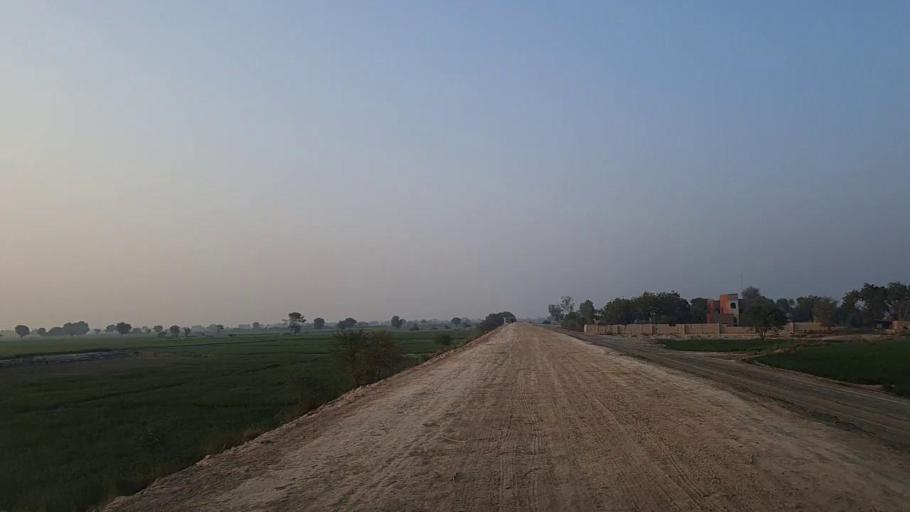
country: PK
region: Sindh
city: Sann
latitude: 26.1921
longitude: 68.0901
